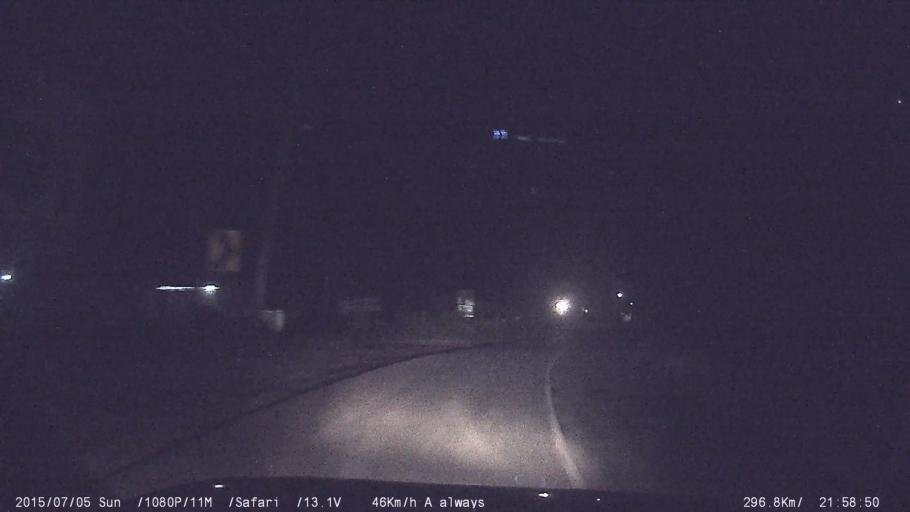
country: IN
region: Kerala
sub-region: Palakkad district
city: Mannarakkat
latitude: 10.9554
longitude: 76.5106
